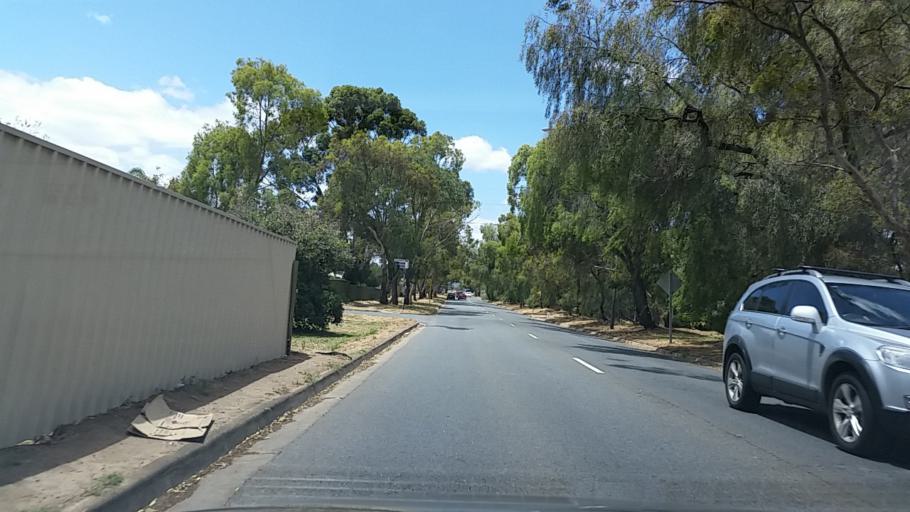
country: AU
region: South Australia
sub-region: Salisbury
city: Salisbury
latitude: -34.7679
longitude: 138.6078
